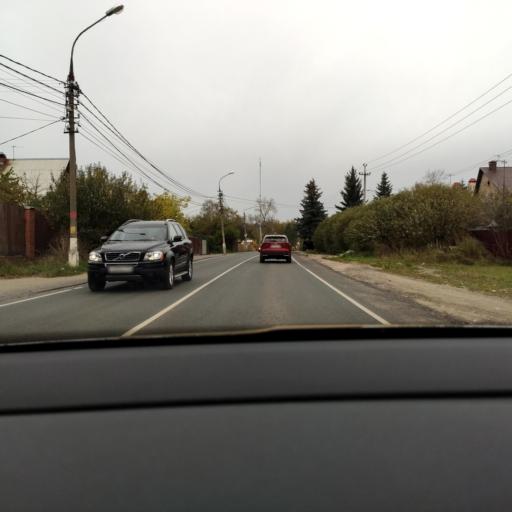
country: RU
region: Moskovskaya
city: Ivanteyevka
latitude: 55.9836
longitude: 37.9317
